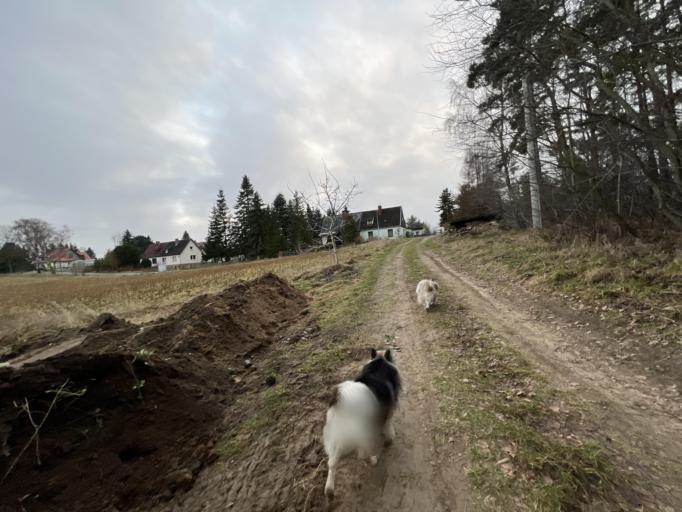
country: DE
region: Mecklenburg-Vorpommern
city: Plau am See
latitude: 53.4922
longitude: 12.2743
